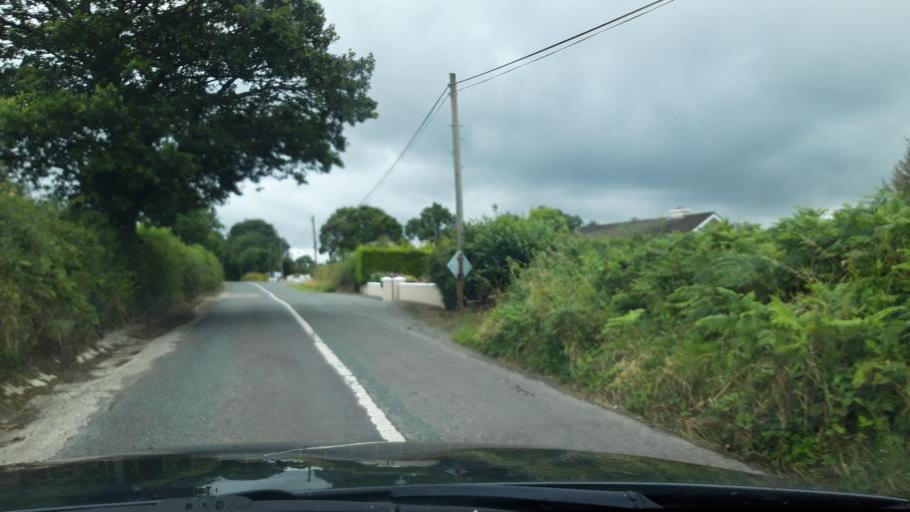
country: IE
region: Munster
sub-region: County Cork
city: Castlemartyr
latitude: 52.1317
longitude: -7.9938
